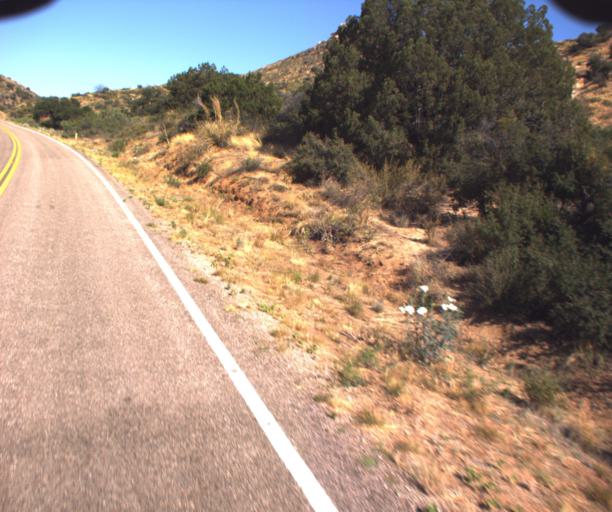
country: US
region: Arizona
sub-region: Graham County
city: Swift Trail Junction
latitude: 32.5746
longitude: -109.8357
